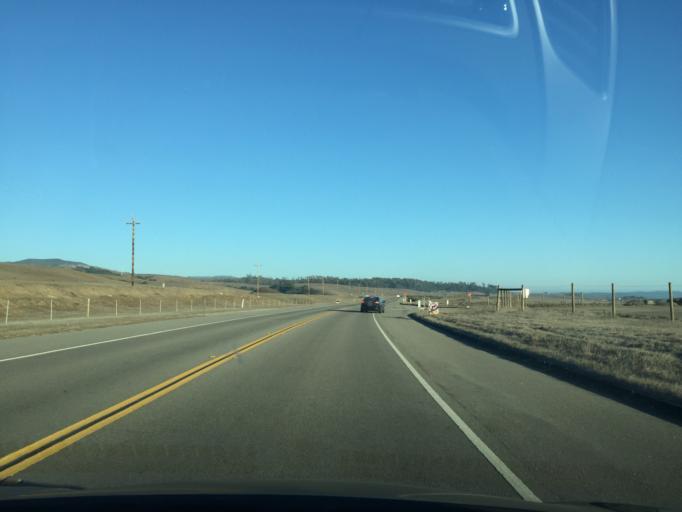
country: US
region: California
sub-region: San Luis Obispo County
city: Cambria
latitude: 35.6404
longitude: -121.1745
